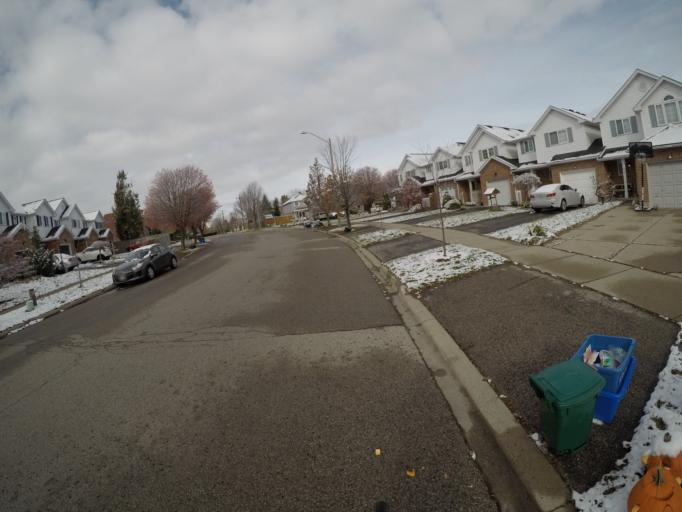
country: CA
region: Ontario
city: Waterloo
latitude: 43.4901
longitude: -80.4909
